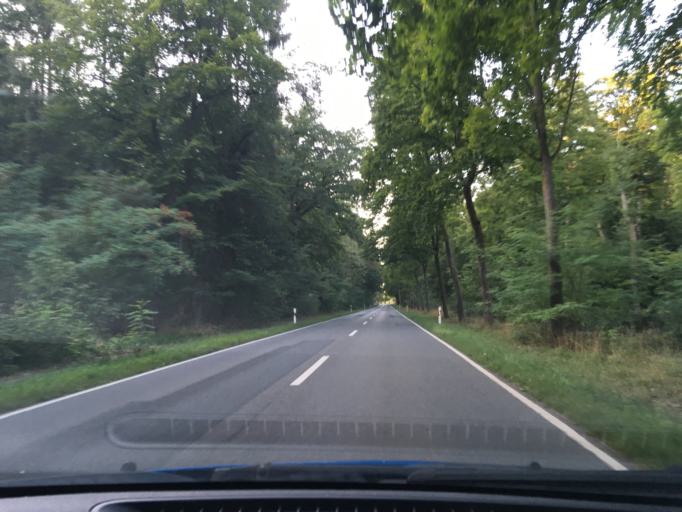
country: DE
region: Lower Saxony
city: Bleckede
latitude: 53.2756
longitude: 10.7424
